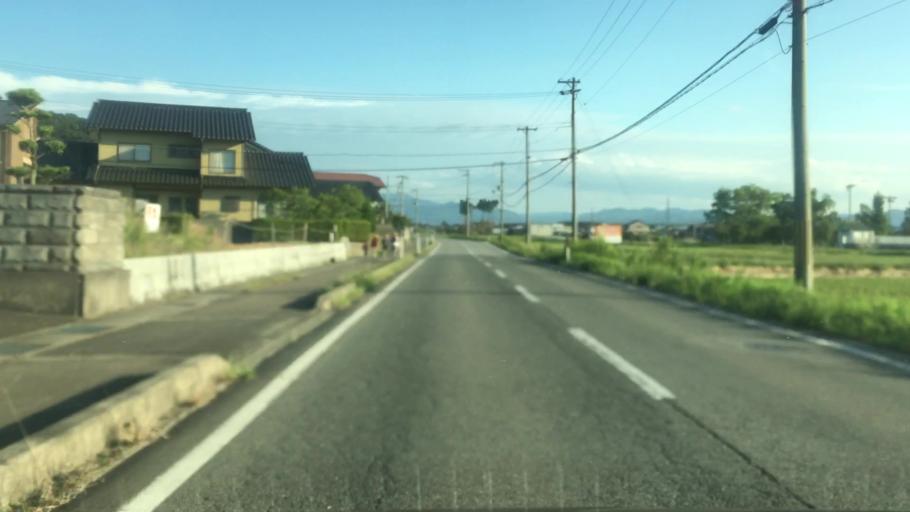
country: JP
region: Hyogo
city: Toyooka
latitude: 35.5643
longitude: 134.8204
